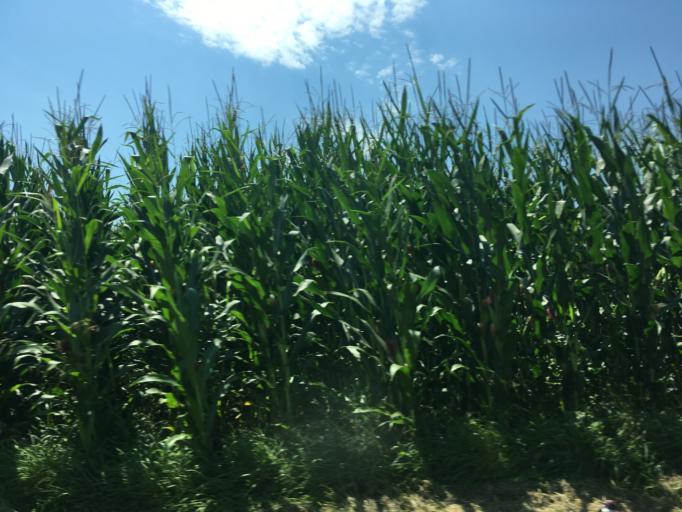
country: SI
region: Metlika
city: Metlika
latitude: 45.6038
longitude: 15.3332
